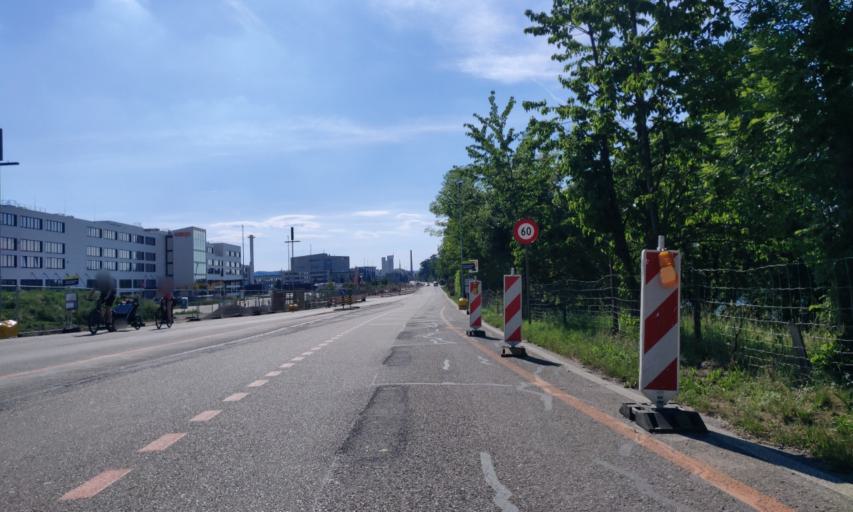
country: CH
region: Basel-Landschaft
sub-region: Bezirk Liestal
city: Pratteln
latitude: 47.5313
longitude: 7.6924
